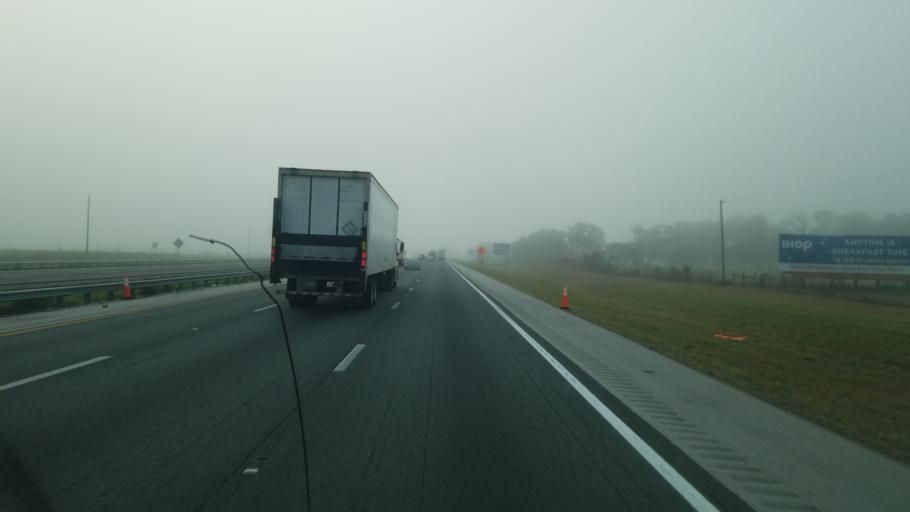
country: US
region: Florida
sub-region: Sumter County
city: Wildwood
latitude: 28.8899
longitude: -82.0984
